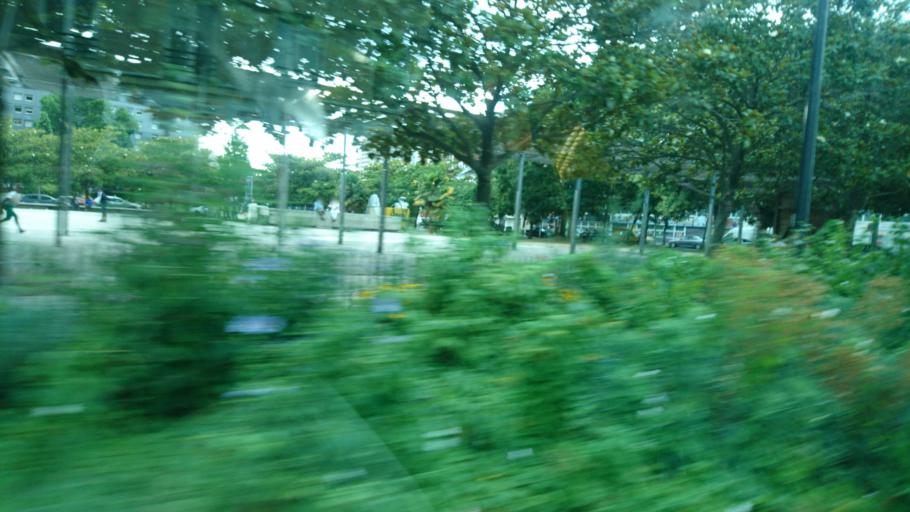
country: FR
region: Ile-de-France
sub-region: Departement de Seine-Saint-Denis
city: Saint-Denis
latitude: 48.9396
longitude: 2.3564
